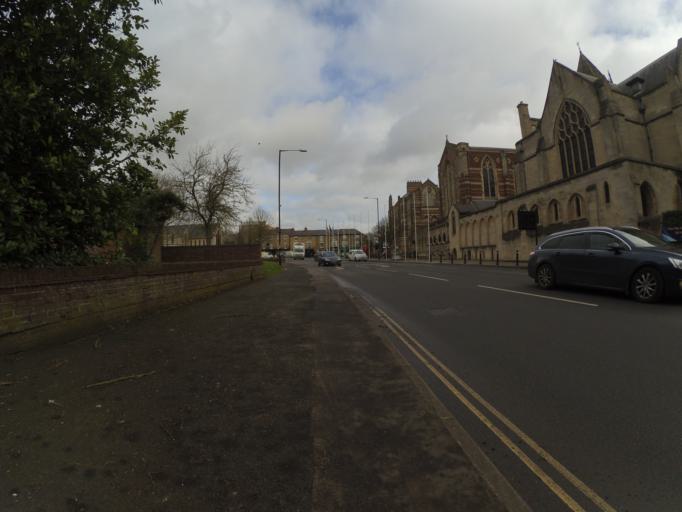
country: GB
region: England
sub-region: Warwickshire
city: Rugby
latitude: 52.3701
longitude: -1.2646
